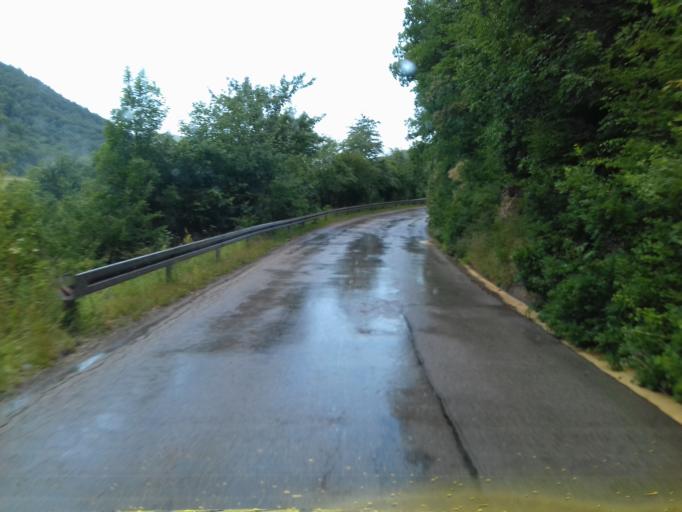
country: BA
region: Federation of Bosnia and Herzegovina
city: Visoko
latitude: 43.9549
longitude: 18.1498
